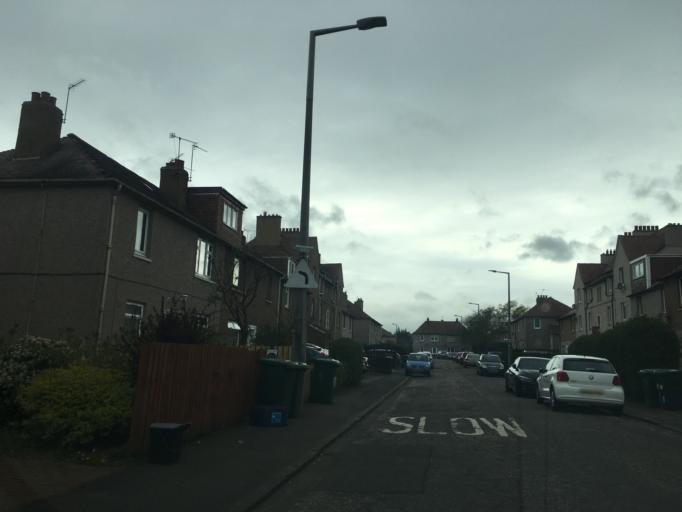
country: GB
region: Scotland
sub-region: Edinburgh
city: Colinton
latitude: 55.9243
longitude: -3.2707
